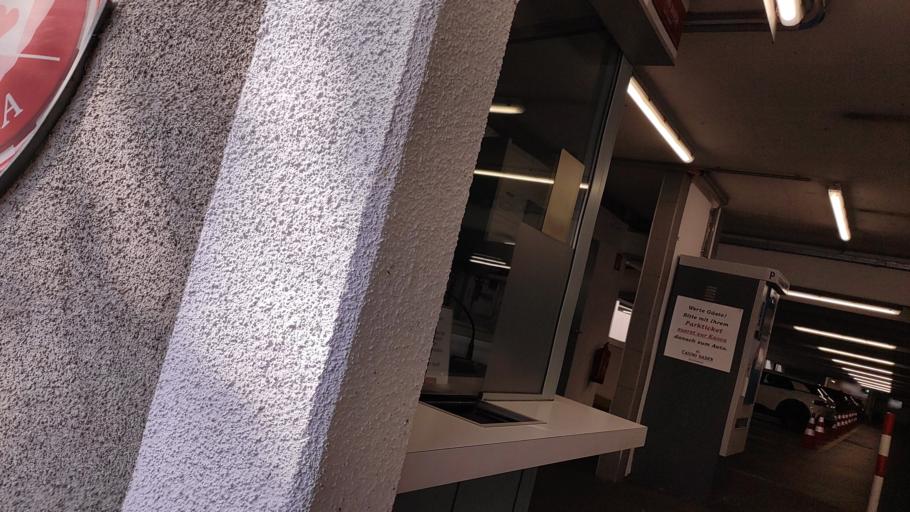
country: AT
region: Lower Austria
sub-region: Politischer Bezirk Baden
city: Baden
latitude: 48.0102
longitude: 16.2313
